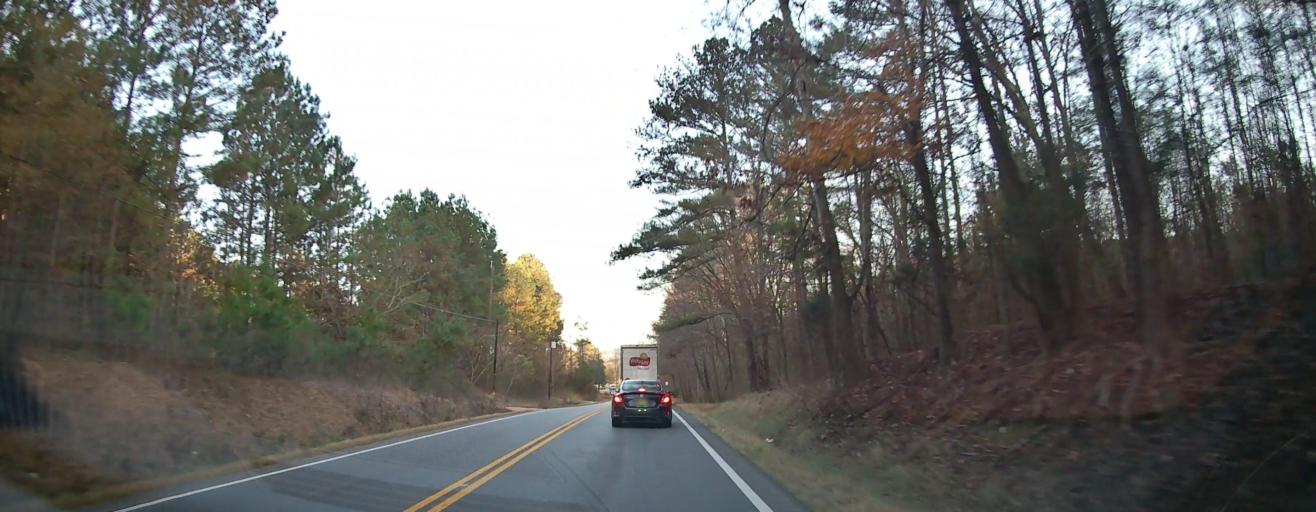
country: US
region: Alabama
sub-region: Saint Clair County
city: Steele
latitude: 34.0711
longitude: -86.3138
